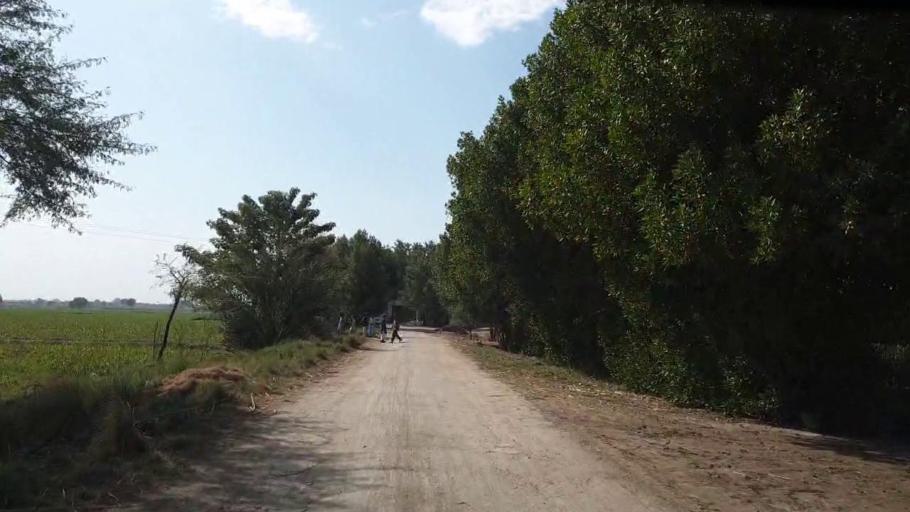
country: PK
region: Sindh
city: Matiari
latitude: 25.5591
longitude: 68.4577
